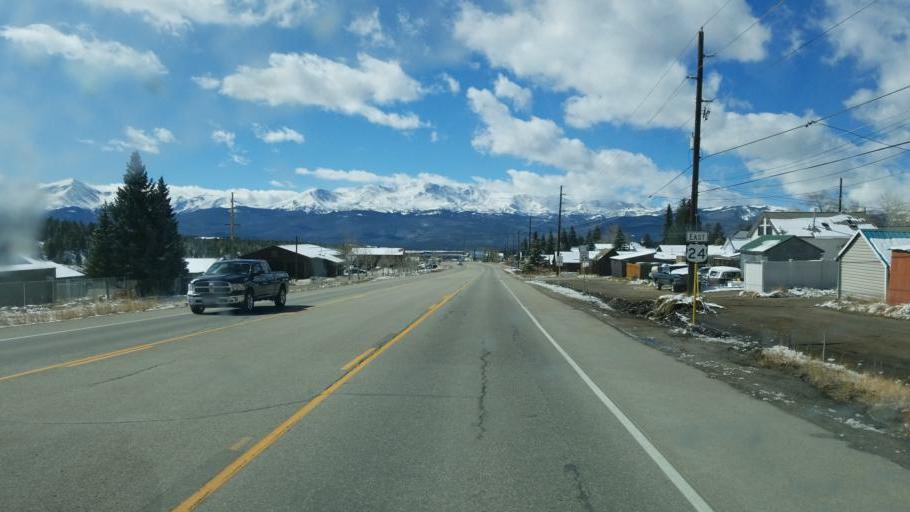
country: US
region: Colorado
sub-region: Lake County
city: Leadville
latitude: 39.2430
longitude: -106.2910
